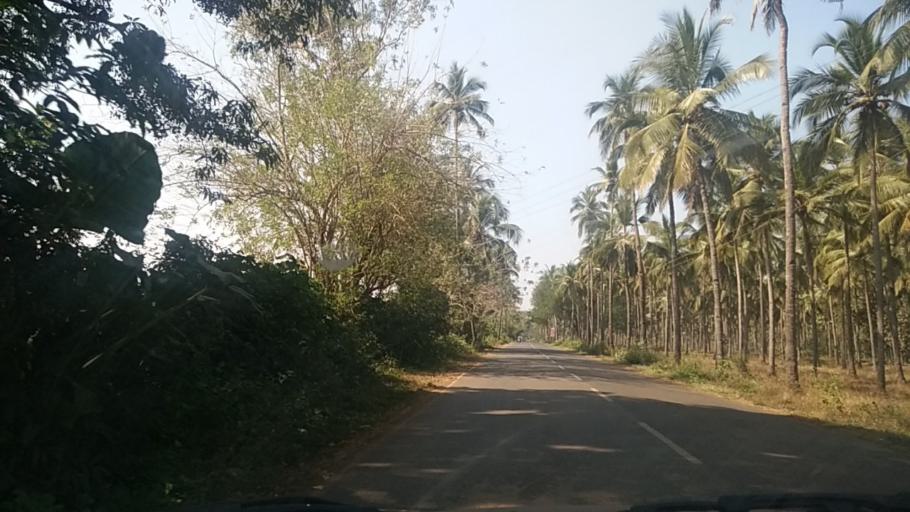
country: IN
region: Goa
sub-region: South Goa
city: Sanguem
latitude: 15.2291
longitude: 74.1799
